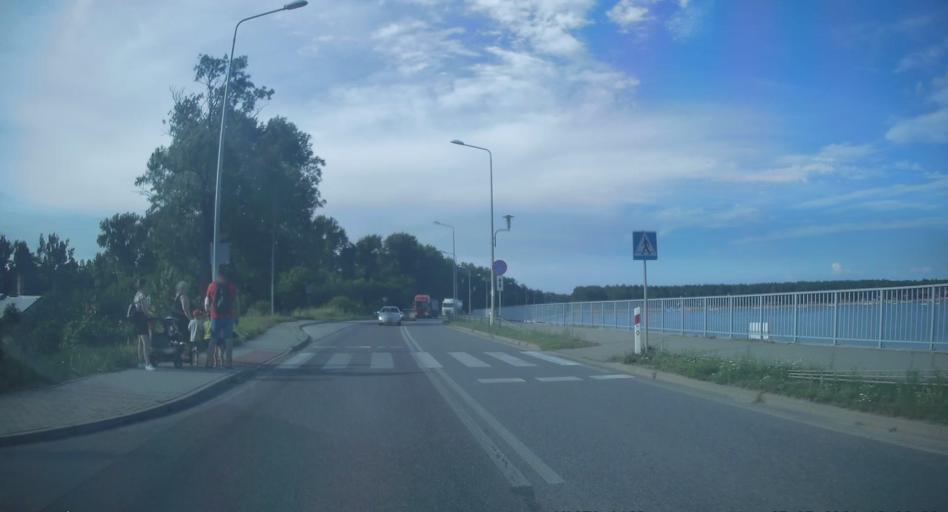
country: PL
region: Swietokrzyskie
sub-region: Powiat konecki
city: Smykow
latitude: 51.1138
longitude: 20.3495
